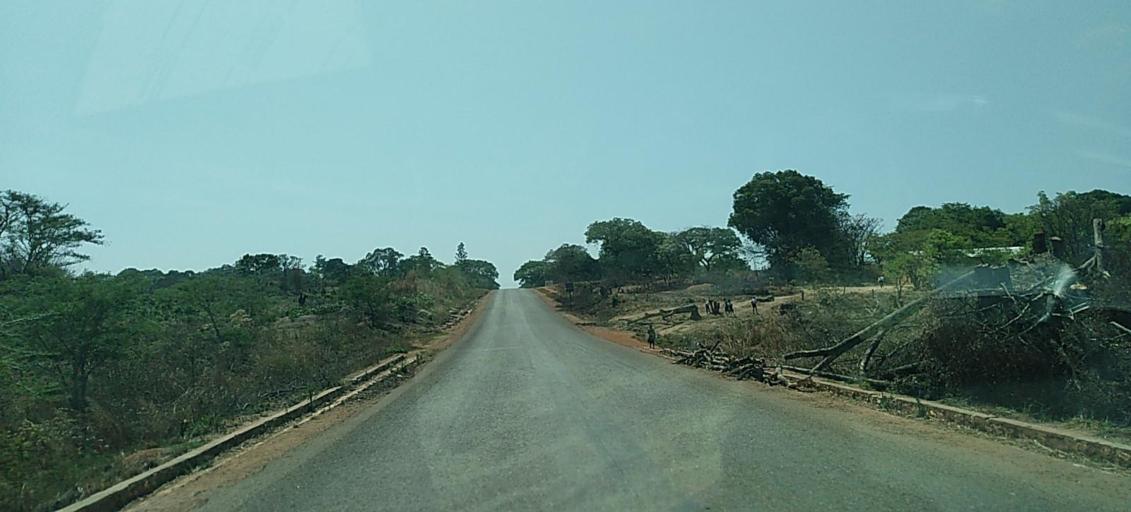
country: ZM
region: North-Western
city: Solwezi
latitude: -12.2738
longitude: 25.6662
